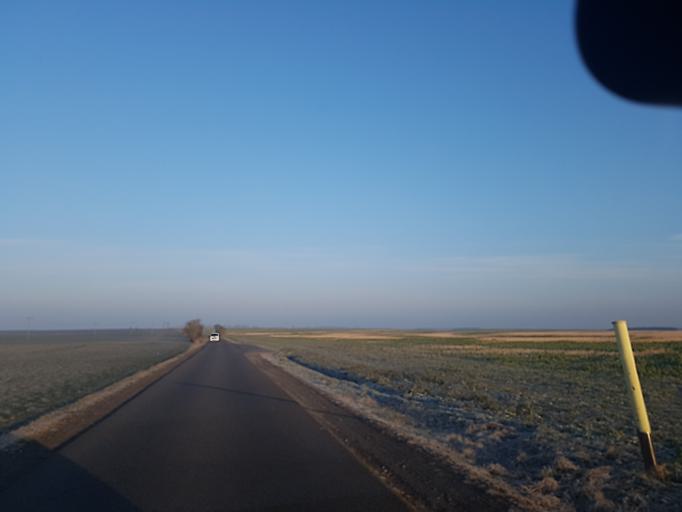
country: DE
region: Brandenburg
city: Niedergorsdorf
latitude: 51.9323
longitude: 13.0265
